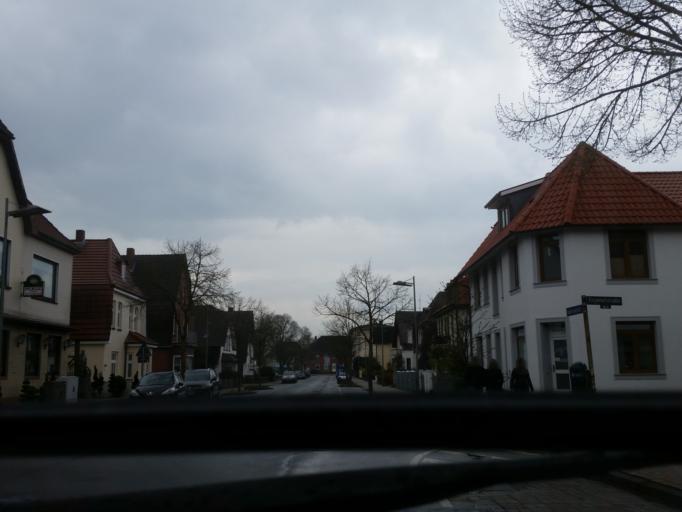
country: DE
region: Lower Saxony
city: Bremervorde
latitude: 53.4847
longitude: 9.1434
